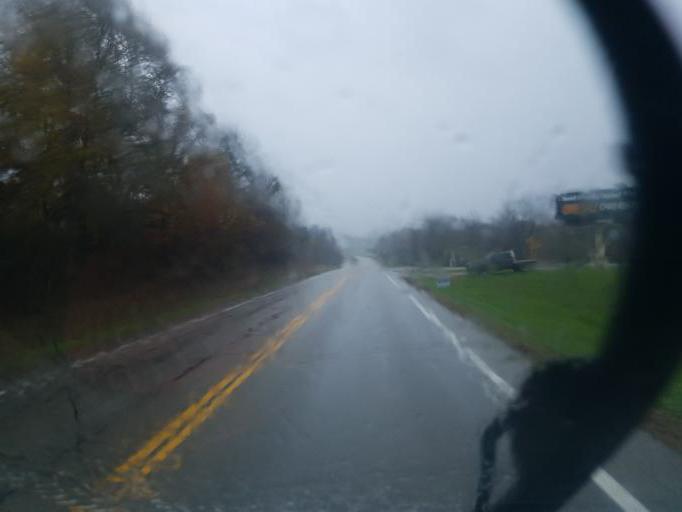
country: US
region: Ohio
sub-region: Muskingum County
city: North Zanesville
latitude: 39.9950
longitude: -82.0697
